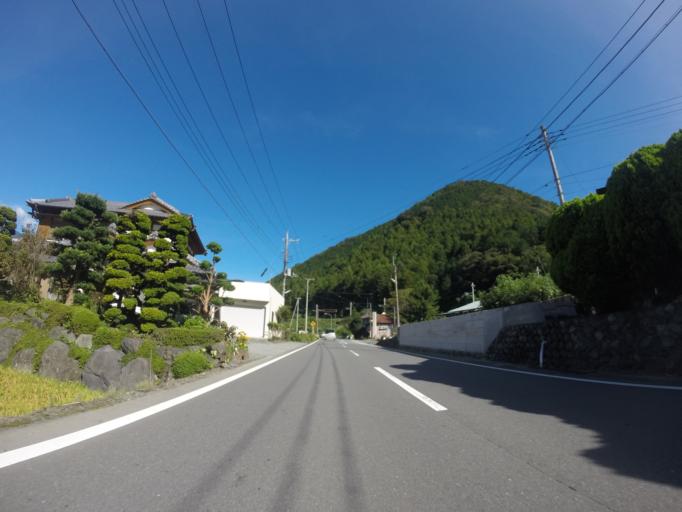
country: JP
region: Shizuoka
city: Fujinomiya
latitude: 35.2920
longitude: 138.4598
